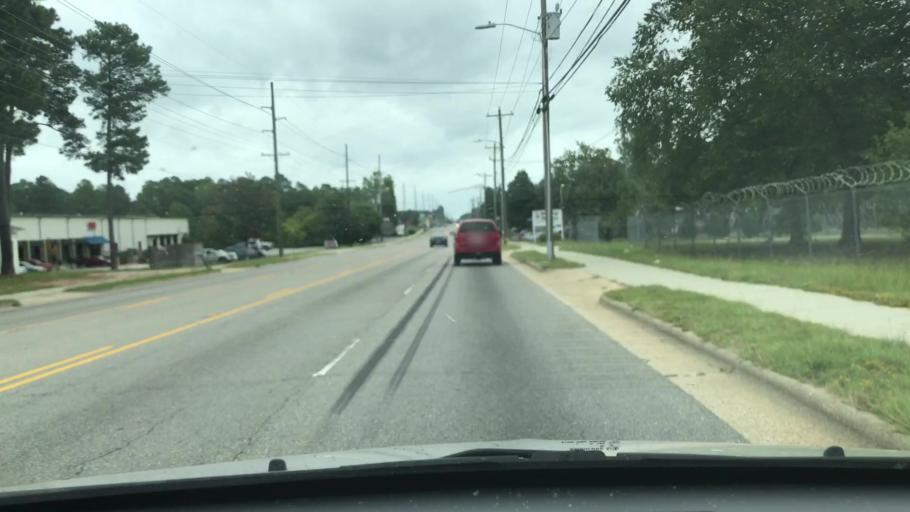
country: US
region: North Carolina
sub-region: Cumberland County
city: Fayetteville
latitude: 35.1030
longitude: -78.9207
